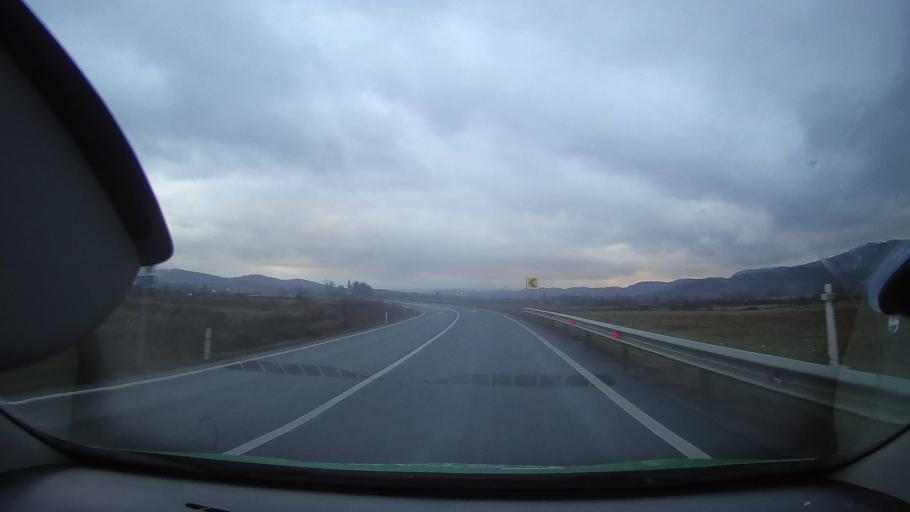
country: RO
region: Hunedoara
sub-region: Comuna Baia de Cris
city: Baia de Cris
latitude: 46.1679
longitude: 22.7425
